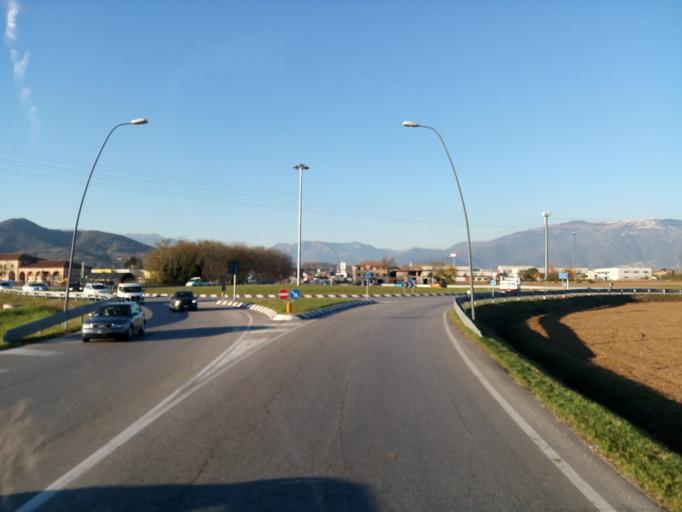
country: IT
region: Veneto
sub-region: Provincia di Treviso
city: Crocetta-Nogare
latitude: 45.8131
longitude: 12.0165
